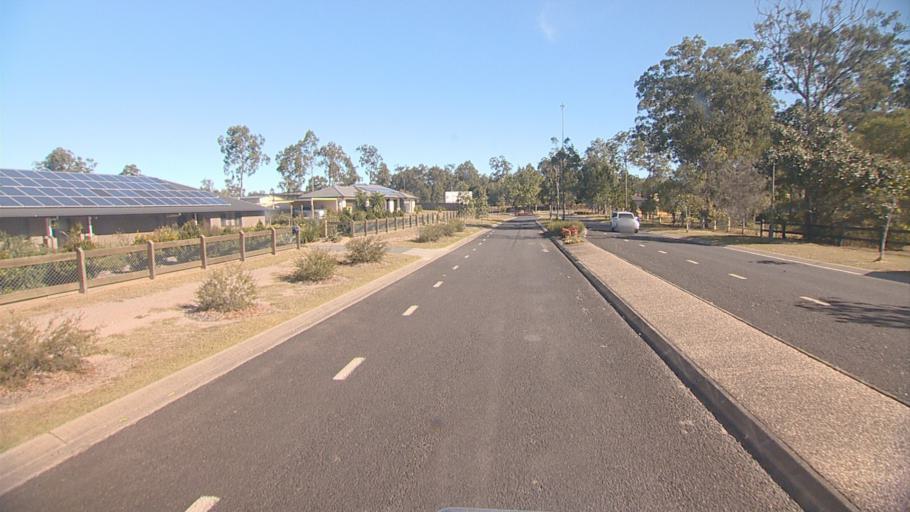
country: AU
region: Queensland
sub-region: Ipswich
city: Springfield Lakes
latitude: -27.7351
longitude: 152.9208
